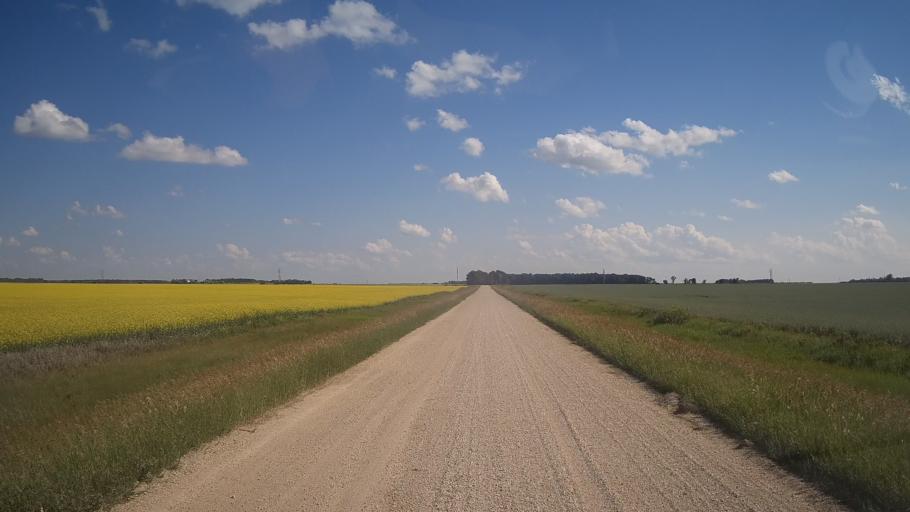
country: CA
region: Manitoba
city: Stonewall
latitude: 50.1291
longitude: -97.5054
